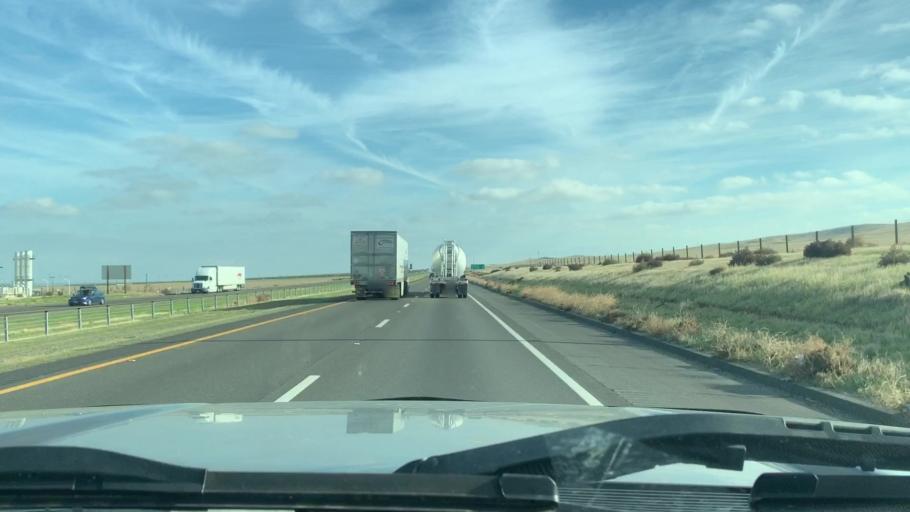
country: US
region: California
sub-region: Kings County
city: Avenal
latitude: 36.0711
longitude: -120.0929
